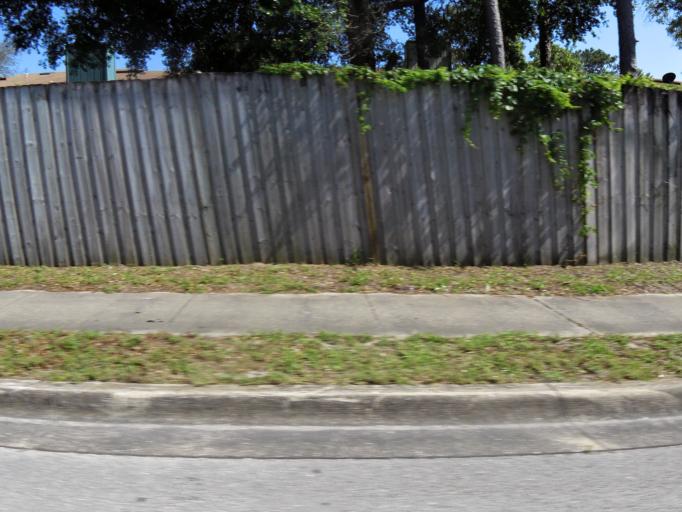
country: US
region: Florida
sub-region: Duval County
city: Atlantic Beach
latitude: 30.3534
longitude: -81.5086
